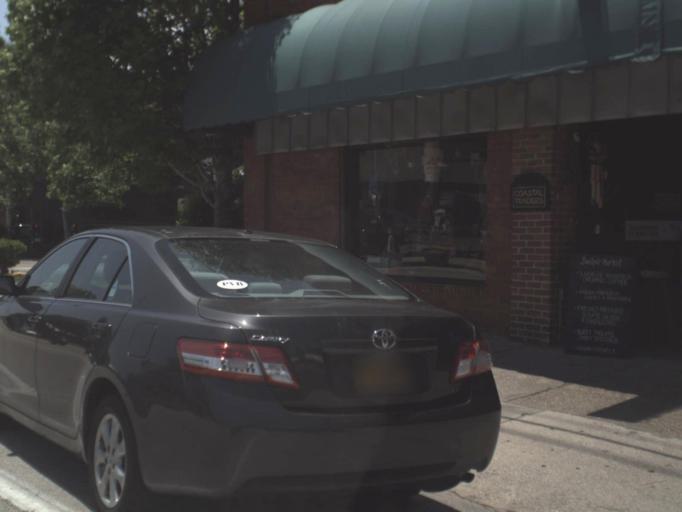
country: US
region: Florida
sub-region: Saint Johns County
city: Saint Augustine
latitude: 29.9016
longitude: -81.3158
